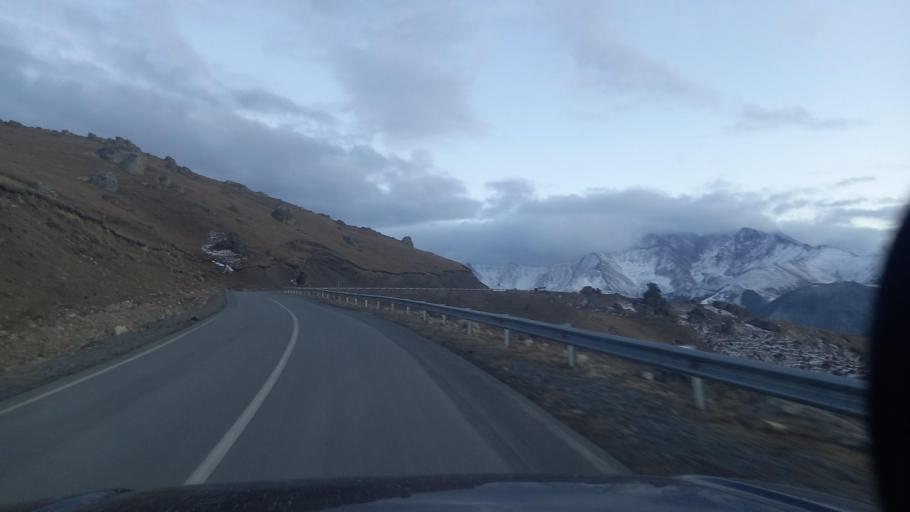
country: RU
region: Ingushetiya
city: Dzhayrakh
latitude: 42.8224
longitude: 44.8290
